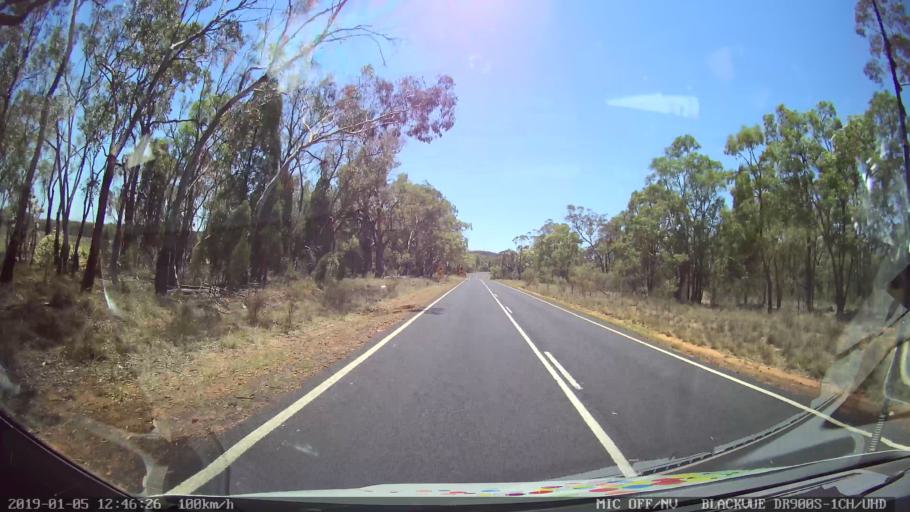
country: AU
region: New South Wales
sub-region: Warrumbungle Shire
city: Coonabarabran
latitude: -31.1179
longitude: 149.5625
